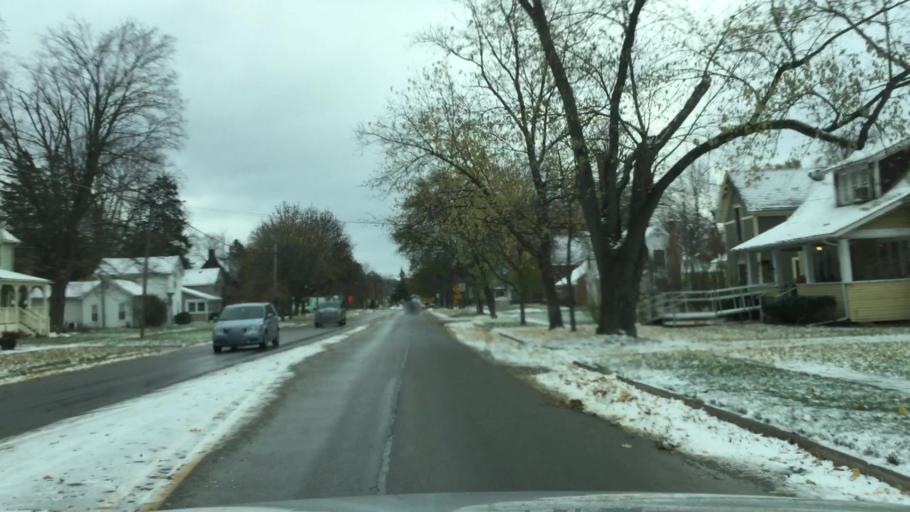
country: US
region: Michigan
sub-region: Livingston County
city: Brighton
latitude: 42.5293
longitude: -83.7908
